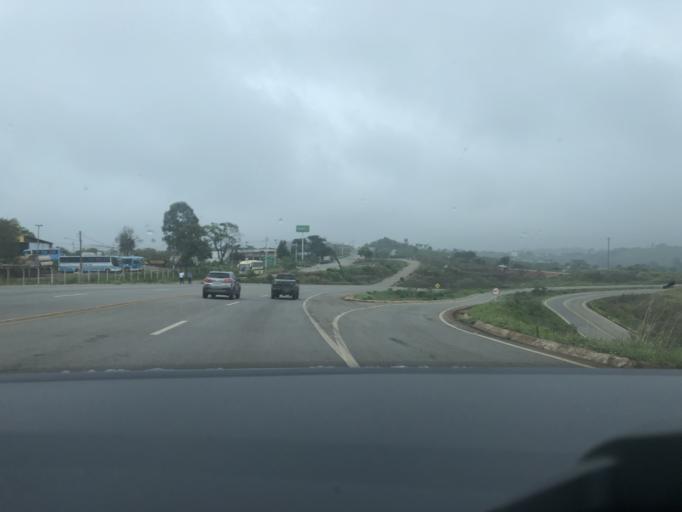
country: BR
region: Minas Gerais
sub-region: Congonhas
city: Congonhas
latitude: -20.6160
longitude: -43.9251
